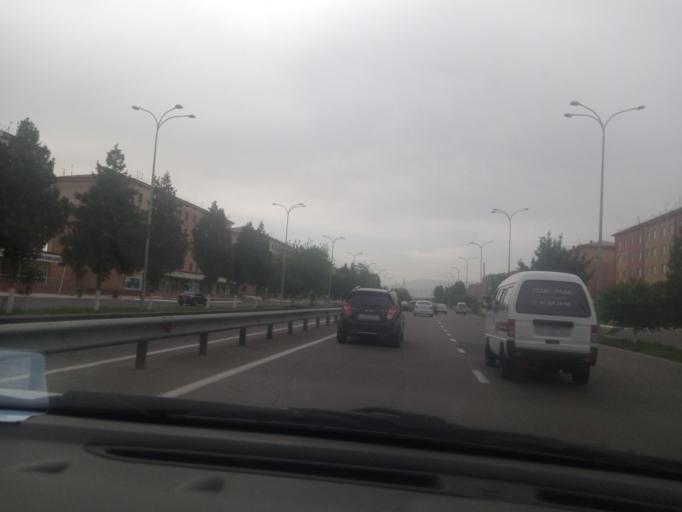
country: UZ
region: Toshkent
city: Ohangaron
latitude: 40.9086
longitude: 69.6259
